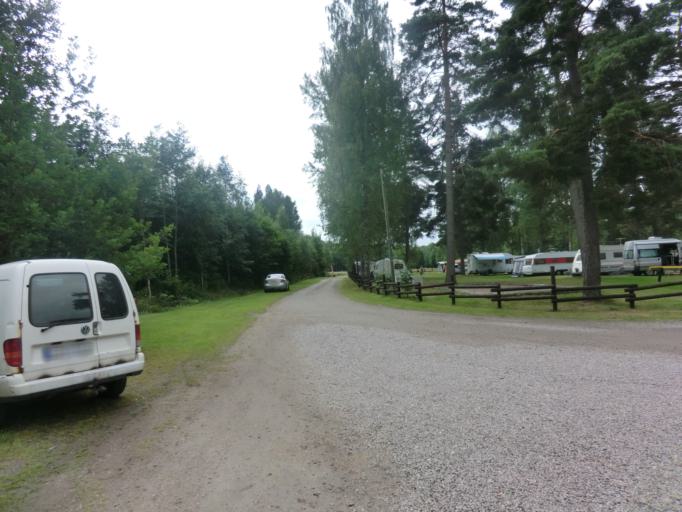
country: SE
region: Vaestra Goetaland
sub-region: Gullspangs Kommun
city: Anderstorp
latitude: 58.9101
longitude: 14.2905
